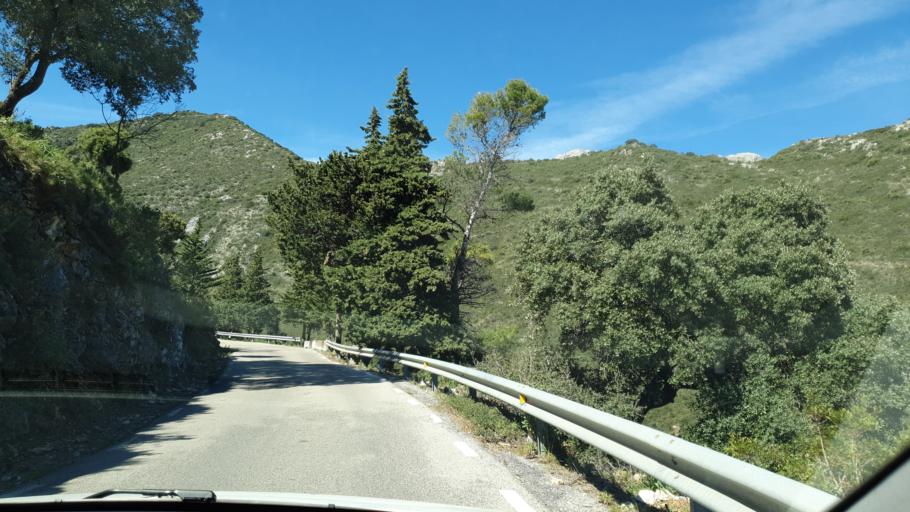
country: ES
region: Andalusia
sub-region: Provincia de Malaga
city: Ojen
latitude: 36.5900
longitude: -4.8757
